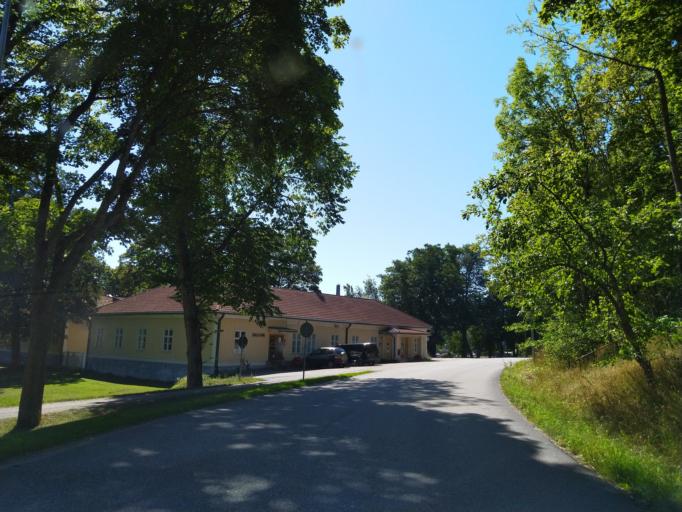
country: FI
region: Varsinais-Suomi
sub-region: Aboland-Turunmaa
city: Dragsfjaerd
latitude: 60.0209
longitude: 22.5059
